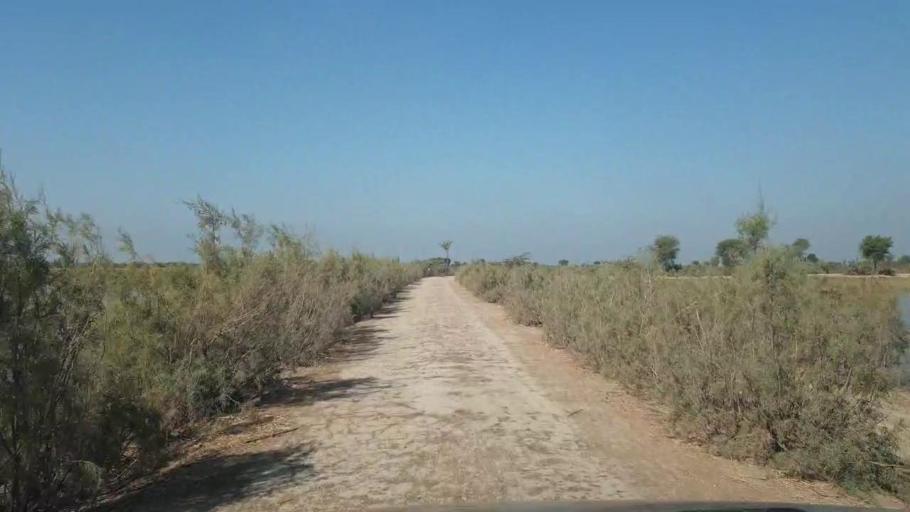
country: PK
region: Sindh
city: Bhit Shah
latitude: 25.8759
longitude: 68.5270
